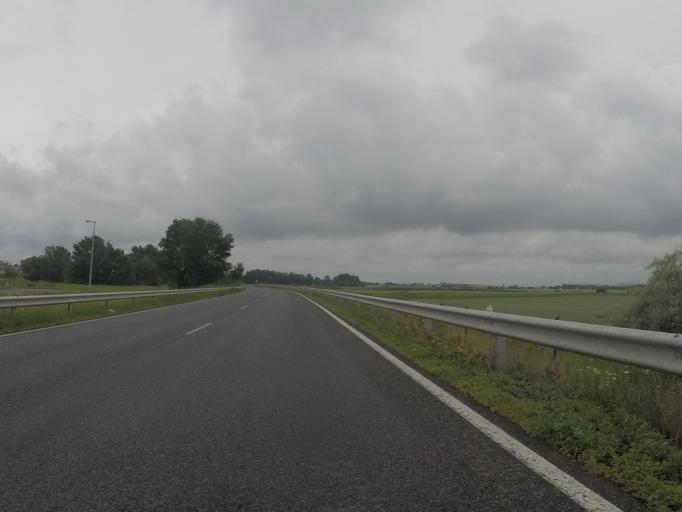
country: HU
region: Gyor-Moson-Sopron
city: Gyorujbarat
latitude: 47.6323
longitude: 17.6626
